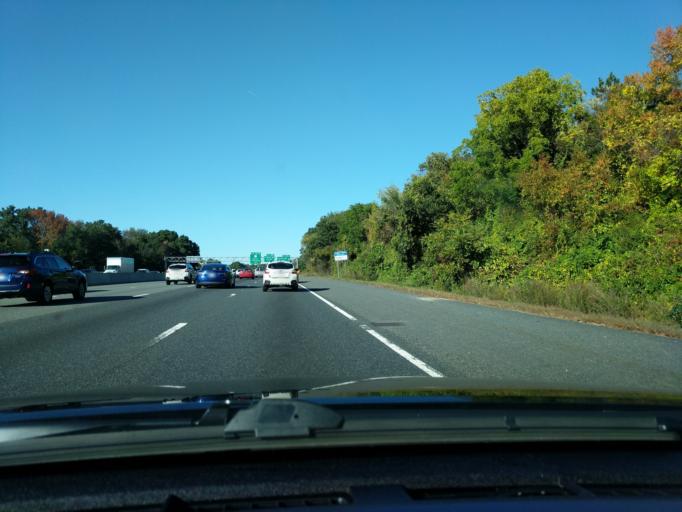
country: US
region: Massachusetts
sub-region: Middlesex County
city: Waltham
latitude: 42.4104
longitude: -71.2580
